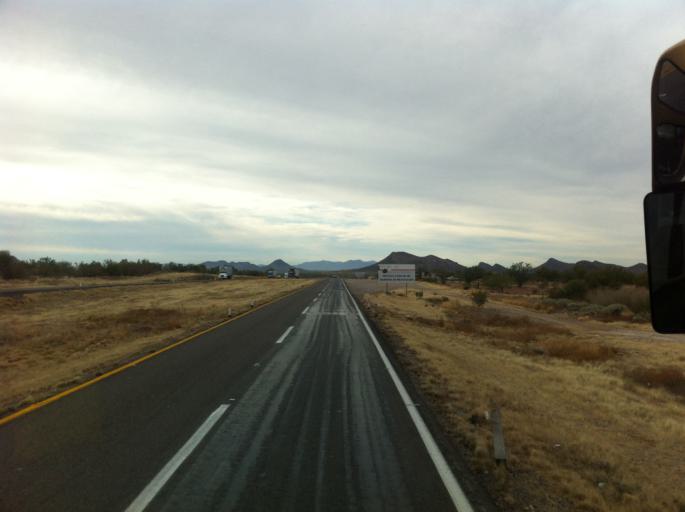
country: MX
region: Sonora
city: Hermosillo
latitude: 28.9509
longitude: -110.9627
